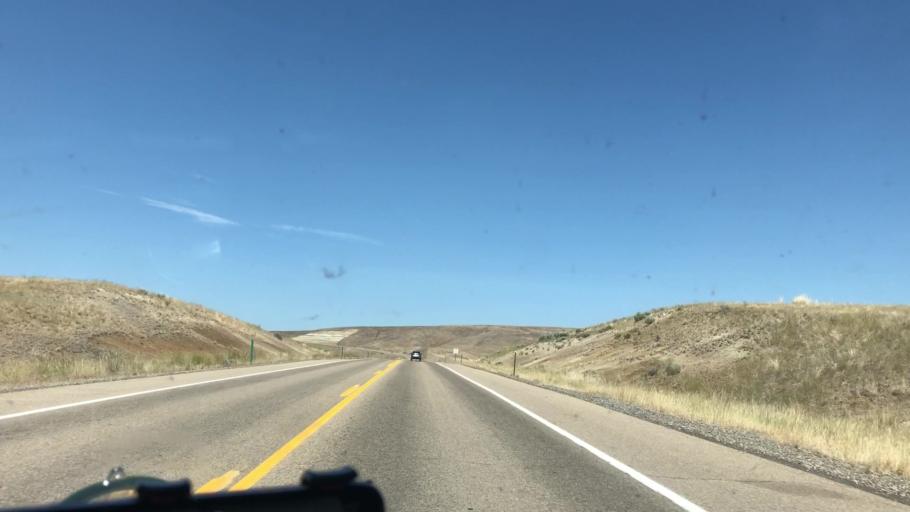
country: US
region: Idaho
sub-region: Owyhee County
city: Marsing
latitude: 43.2759
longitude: -116.9978
